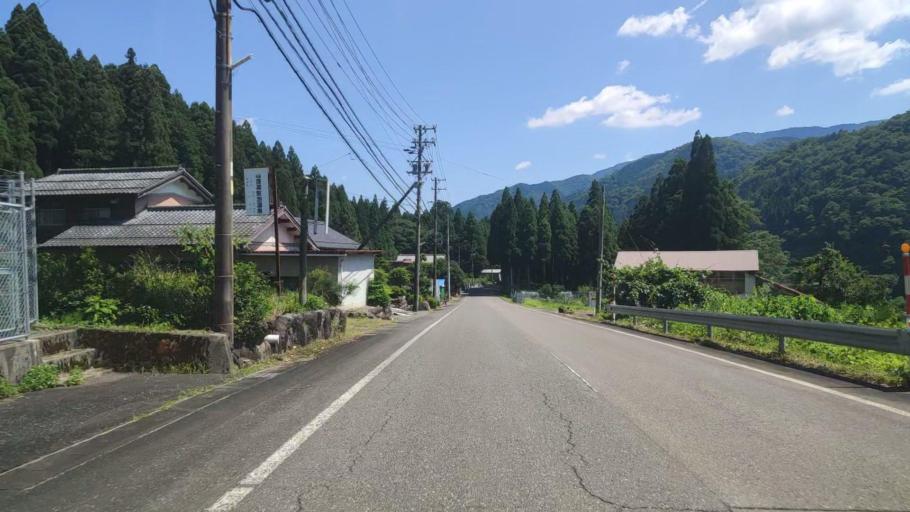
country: JP
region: Gifu
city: Godo
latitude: 35.6668
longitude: 136.5779
